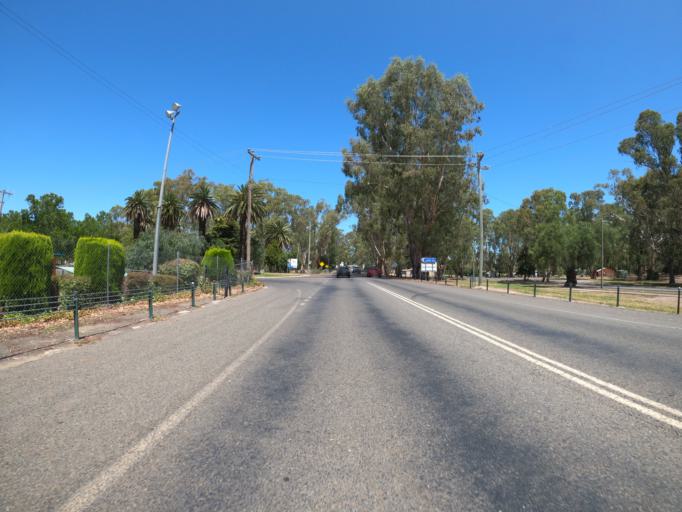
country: AU
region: New South Wales
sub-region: Corowa Shire
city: Corowa
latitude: -36.0041
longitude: 146.3943
